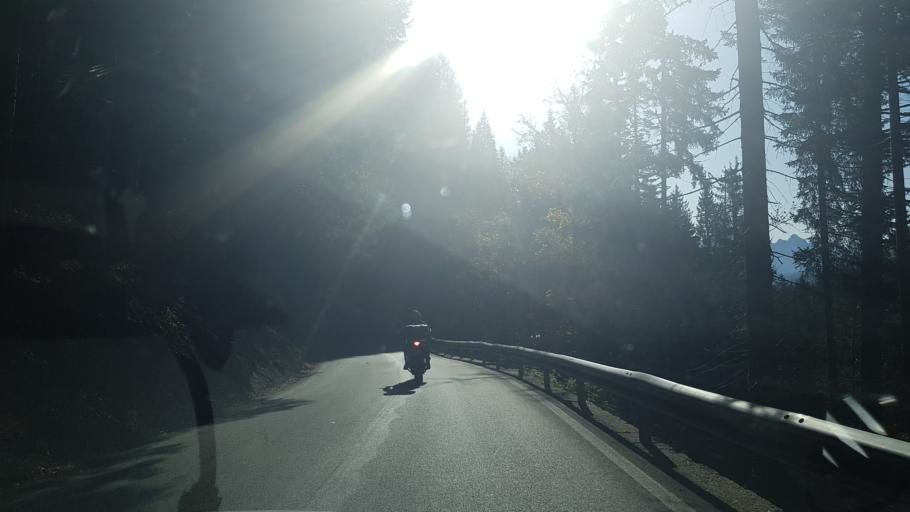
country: IT
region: Veneto
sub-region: Provincia di Belluno
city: Candide
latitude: 46.6425
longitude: 12.4551
